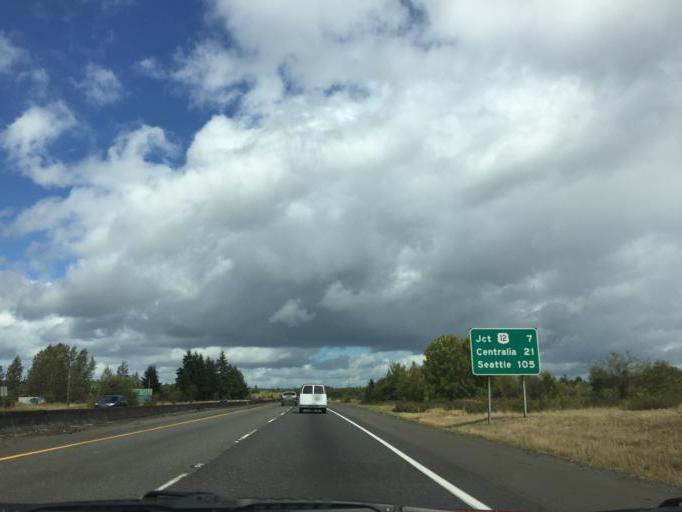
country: US
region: Washington
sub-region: Lewis County
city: Winlock
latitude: 46.4515
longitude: -122.8867
